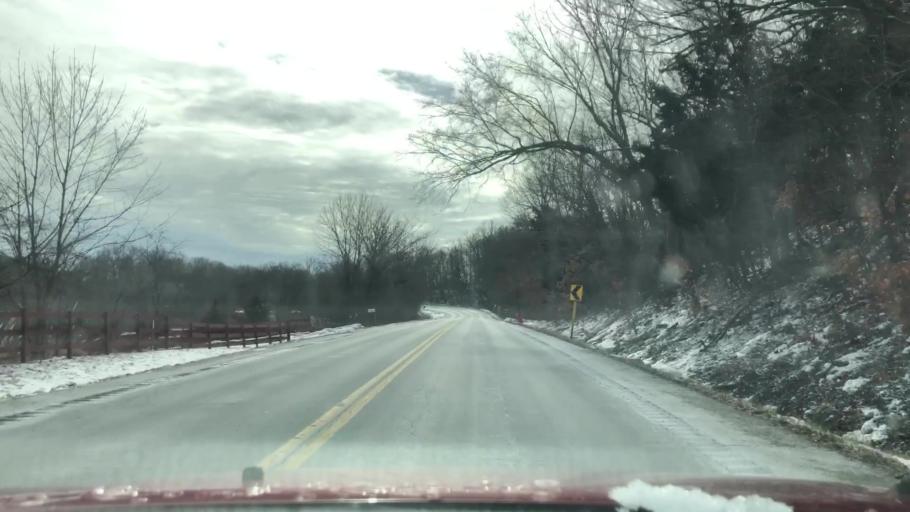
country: US
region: Missouri
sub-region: Jackson County
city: Lone Jack
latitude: 38.8955
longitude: -94.1354
